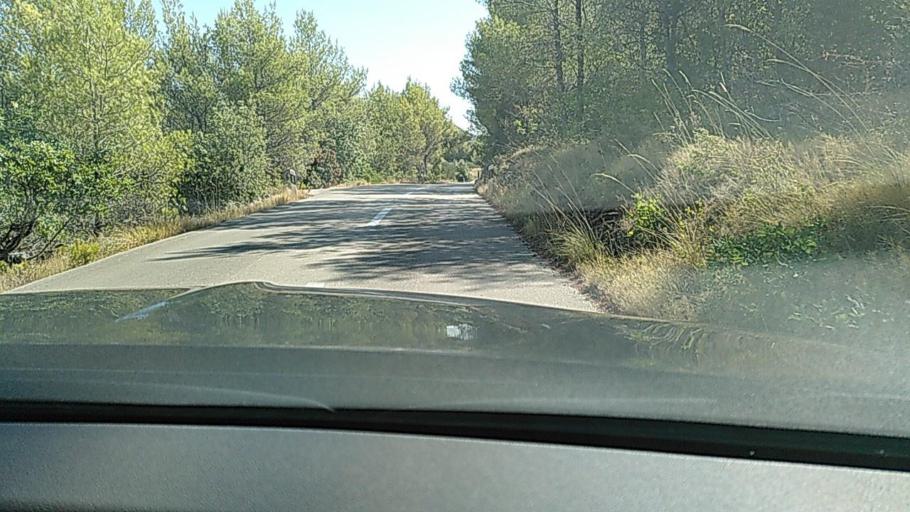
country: HR
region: Splitsko-Dalmatinska
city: Jelsa
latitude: 43.1429
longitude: 16.8132
